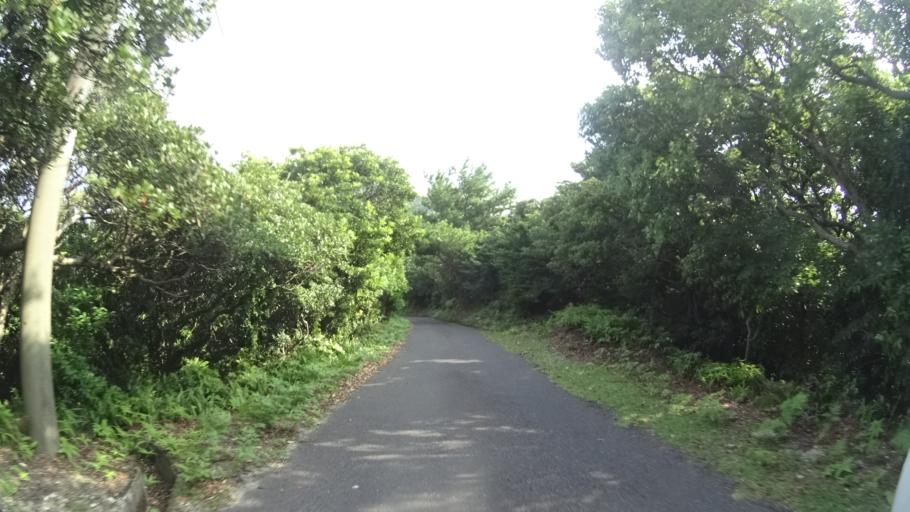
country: JP
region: Kagoshima
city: Nishinoomote
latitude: 30.3912
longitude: 130.3832
